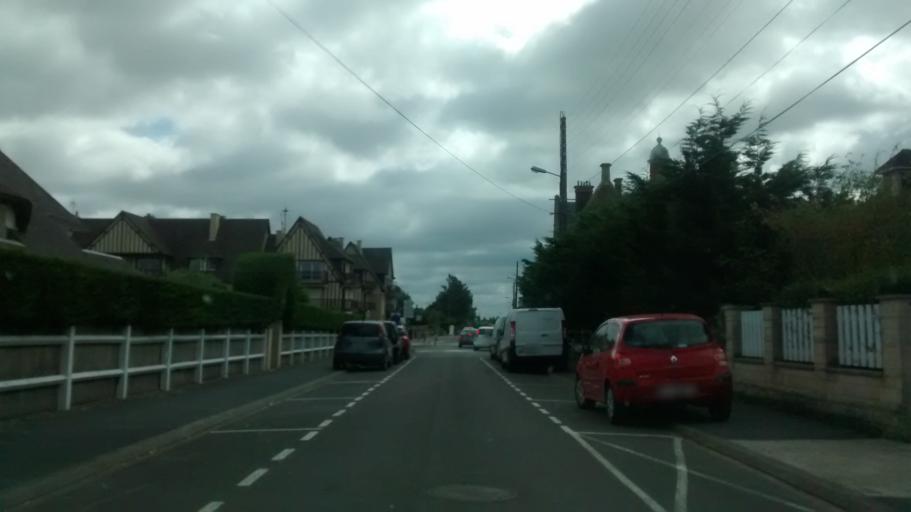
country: FR
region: Lower Normandy
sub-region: Departement du Calvados
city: Ouistreham
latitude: 49.2900
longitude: -0.2653
